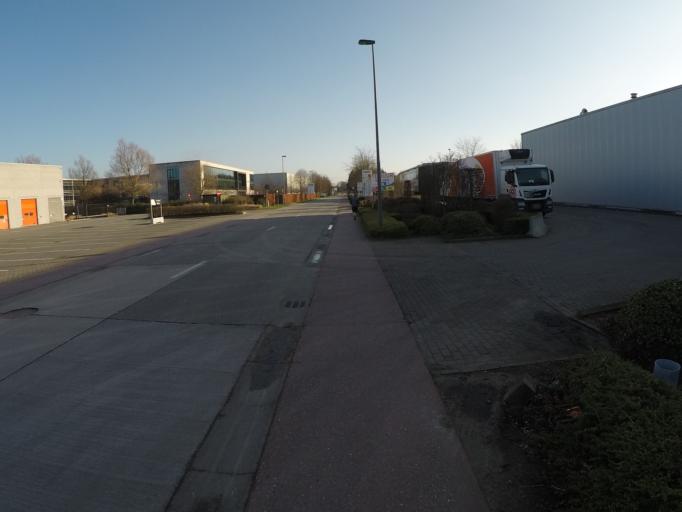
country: BE
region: Flanders
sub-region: Provincie Antwerpen
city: Wommelgem
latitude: 51.2104
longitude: 4.5206
